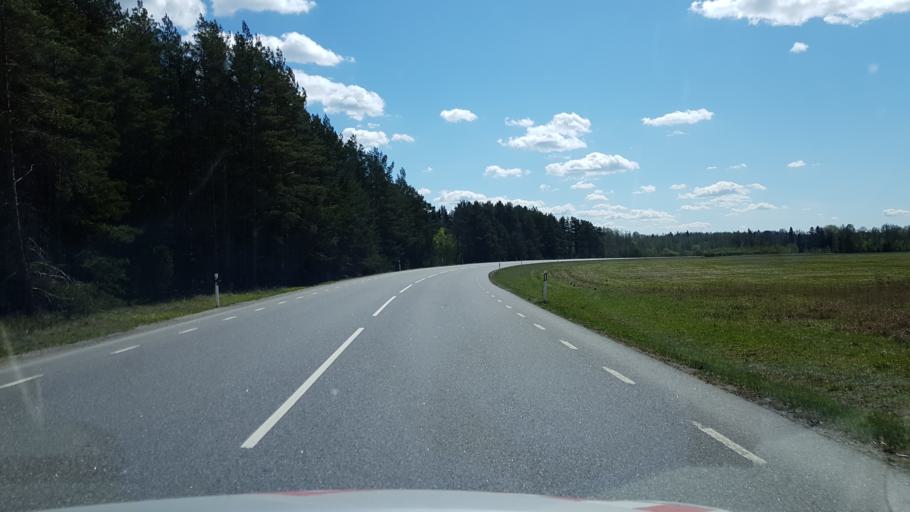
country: EE
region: Harju
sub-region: Paldiski linn
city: Paldiski
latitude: 59.2569
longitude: 24.1526
